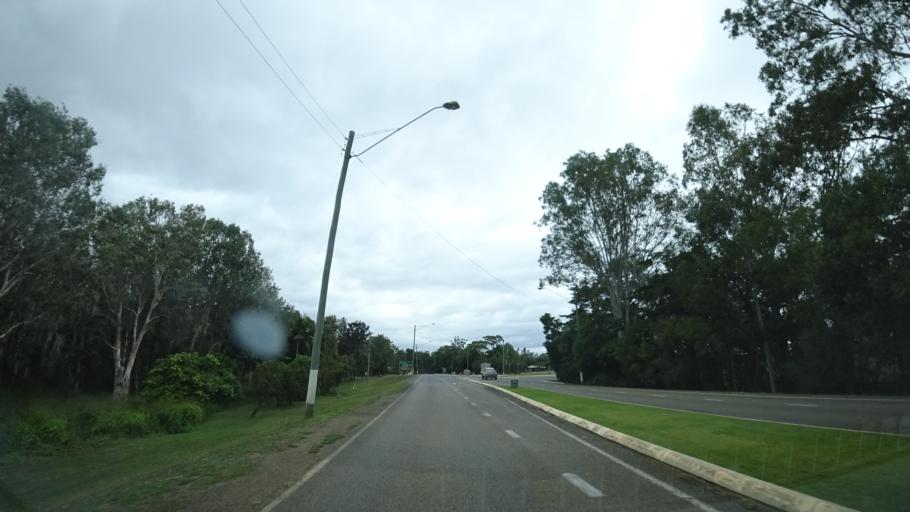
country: AU
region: Queensland
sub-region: Tablelands
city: Mareeba
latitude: -16.9838
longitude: 145.4180
